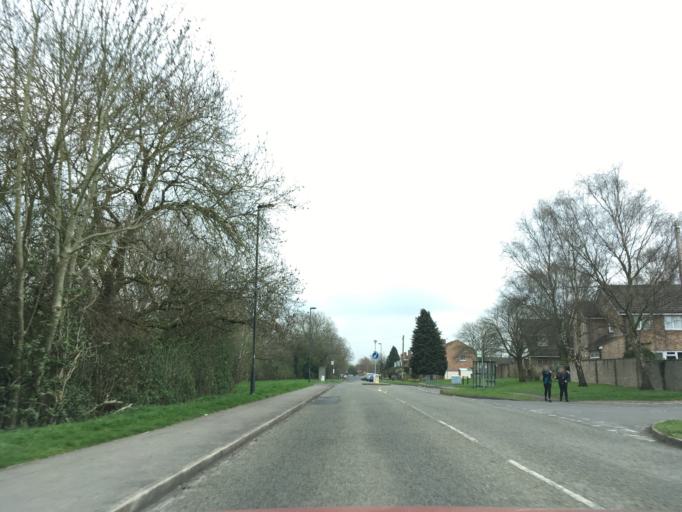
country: GB
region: England
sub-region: South Gloucestershire
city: Stoke Gifford
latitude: 51.5322
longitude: -2.5568
